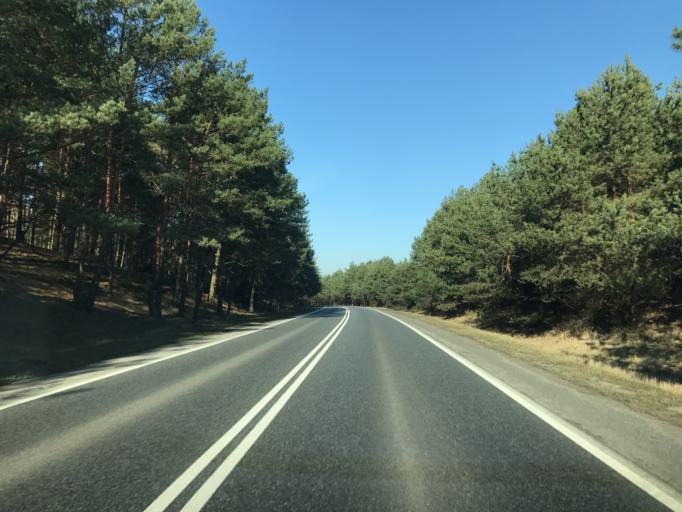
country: PL
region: Kujawsko-Pomorskie
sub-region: Powiat bydgoski
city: Solec Kujawski
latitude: 53.0732
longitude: 18.1504
